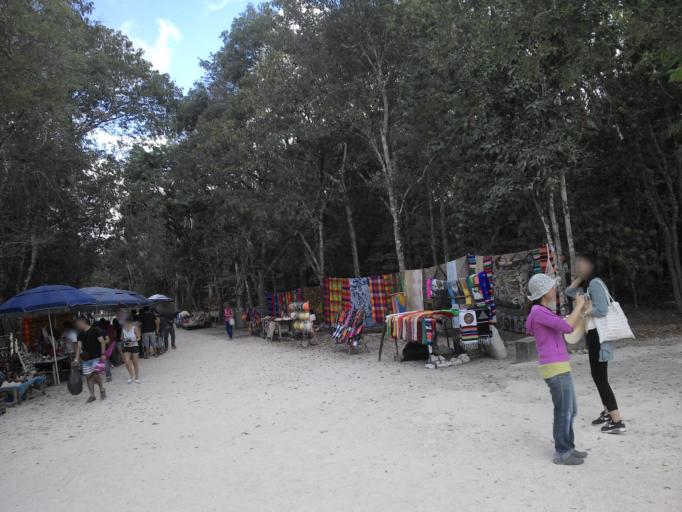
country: MX
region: Yucatan
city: Chichen-Itza
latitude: 20.6841
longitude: -88.5684
